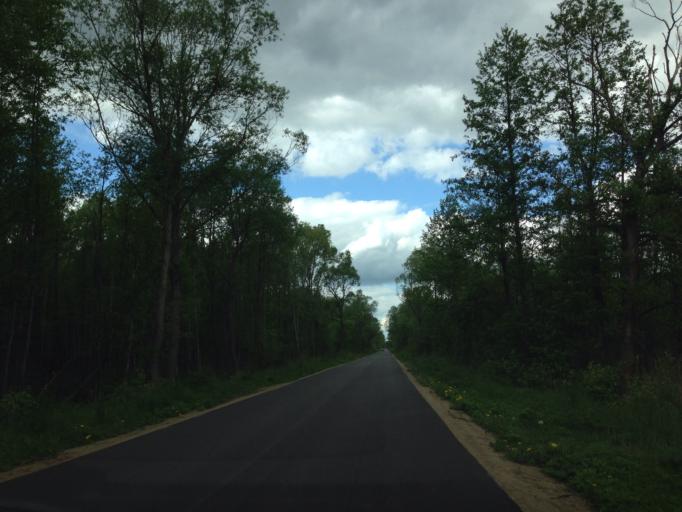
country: PL
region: Podlasie
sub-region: Powiat bialostocki
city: Tykocin
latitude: 53.3018
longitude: 22.6046
